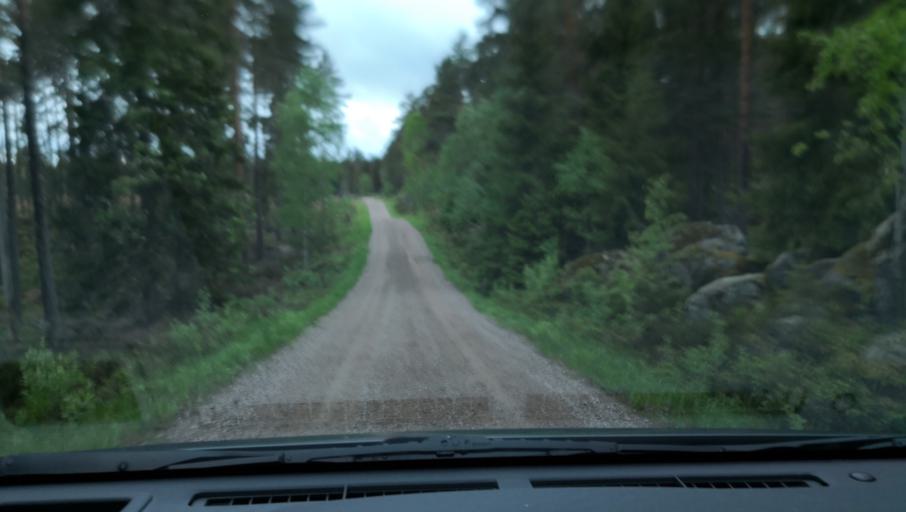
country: SE
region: Uppsala
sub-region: Heby Kommun
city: OEstervala
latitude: 59.9719
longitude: 17.2575
